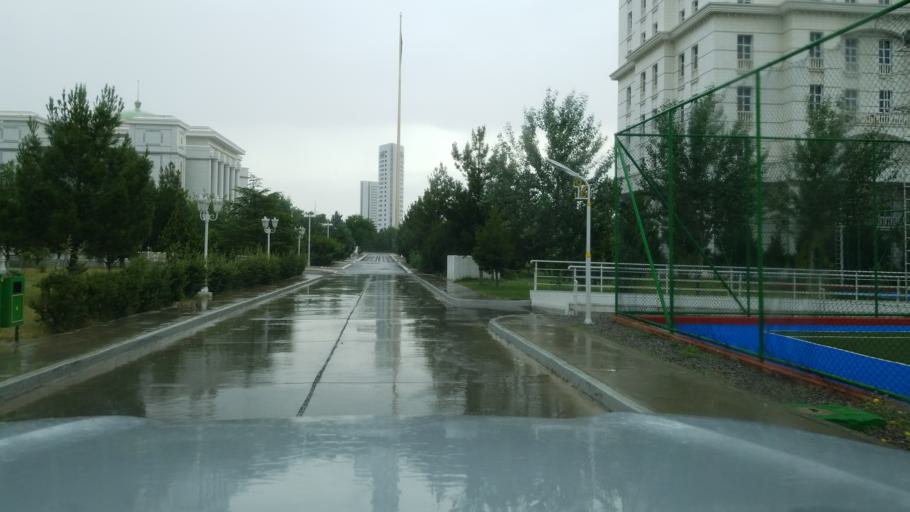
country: TM
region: Ahal
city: Ashgabat
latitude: 37.8850
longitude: 58.3542
